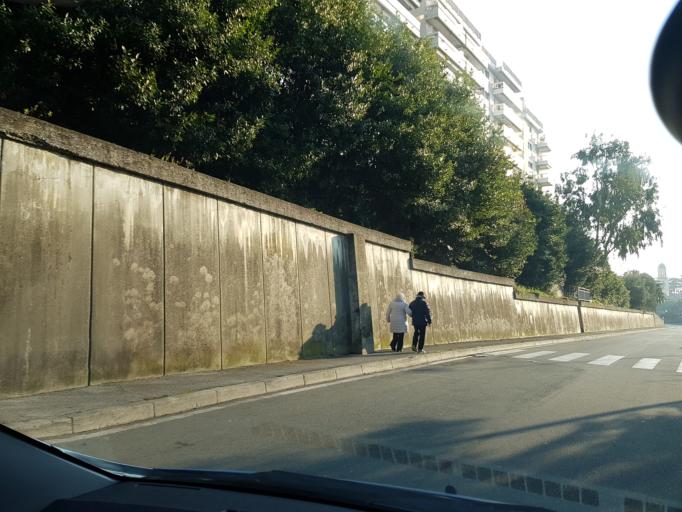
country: IT
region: Liguria
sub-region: Provincia di Genova
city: Bogliasco
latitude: 44.3967
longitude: 9.0057
